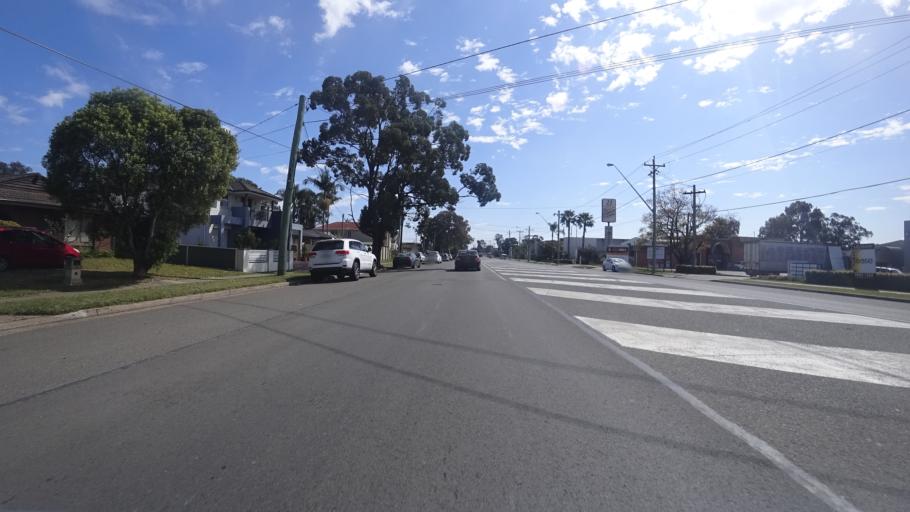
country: AU
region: New South Wales
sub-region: Bankstown
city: Milperra
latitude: -33.9266
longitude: 150.9622
